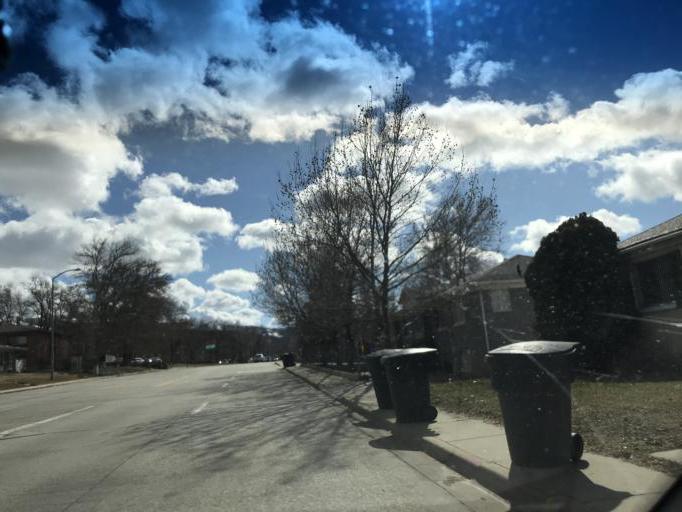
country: US
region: Utah
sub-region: Davis County
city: Bountiful
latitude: 40.8836
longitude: -111.8725
